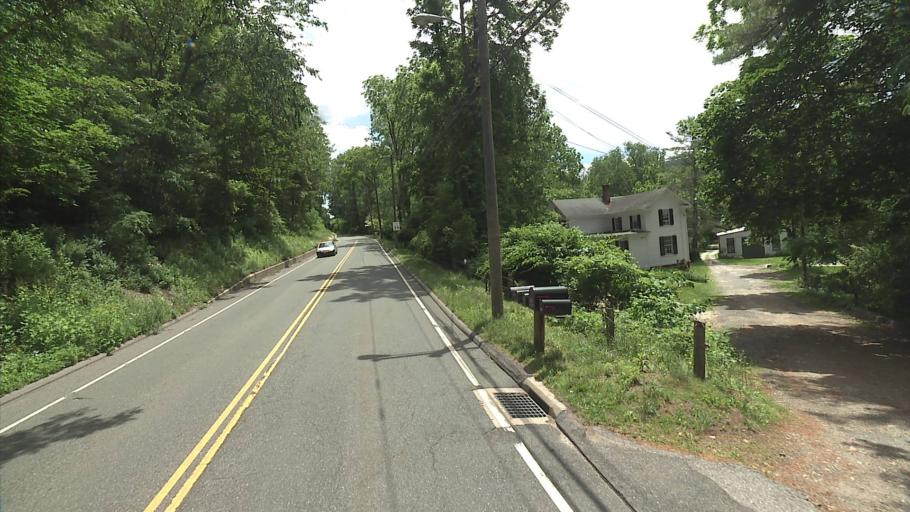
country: US
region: Connecticut
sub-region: Litchfield County
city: Canaan
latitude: 41.9332
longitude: -73.3886
